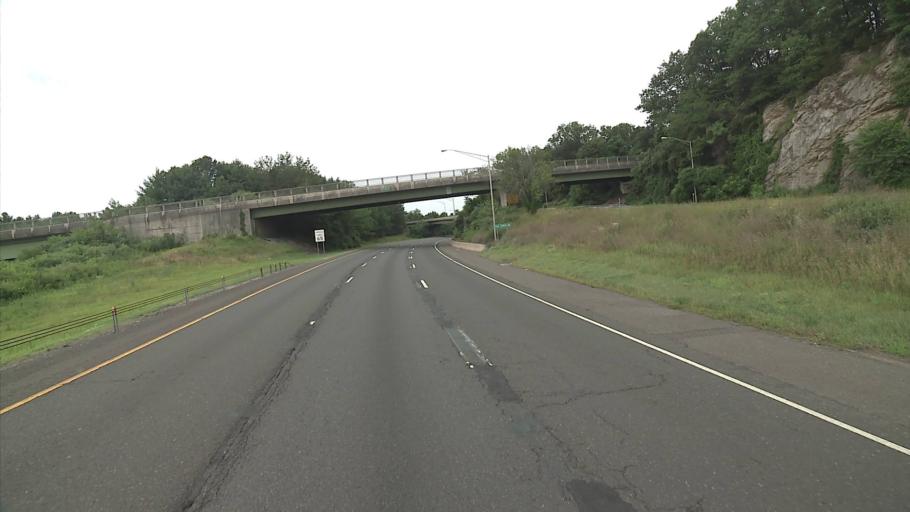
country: US
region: Connecticut
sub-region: Fairfield County
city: Newtown
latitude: 41.4160
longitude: -73.2652
